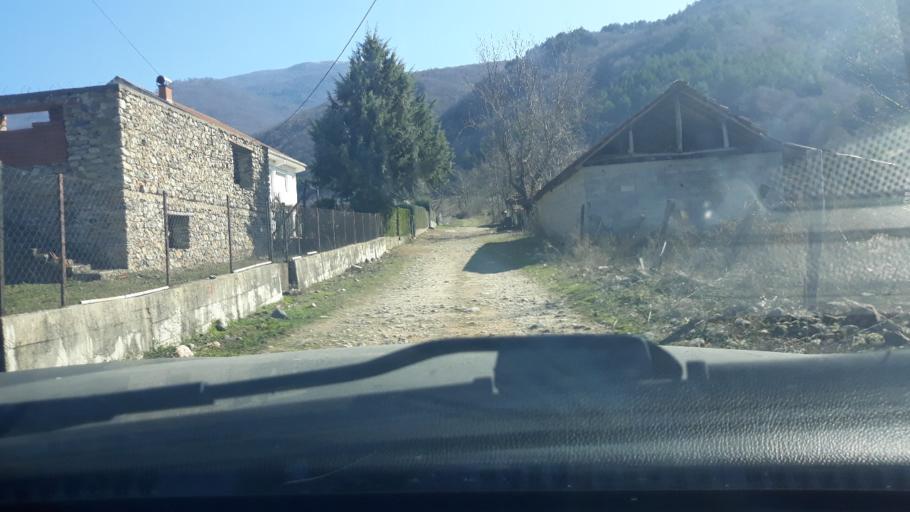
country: MK
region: Novo Selo
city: Susica
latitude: 41.3791
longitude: 22.8179
